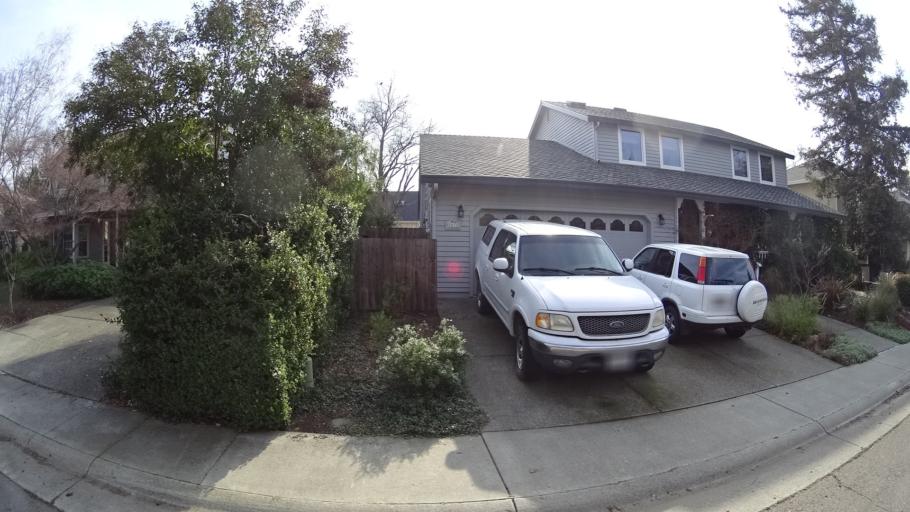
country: US
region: California
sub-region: Yolo County
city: Davis
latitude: 38.5576
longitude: -121.7790
